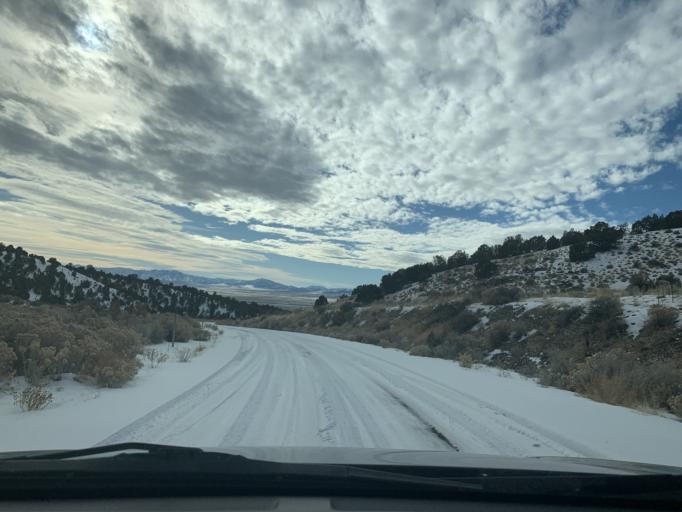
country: US
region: Utah
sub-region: Tooele County
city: Tooele
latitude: 40.3093
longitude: -112.2530
